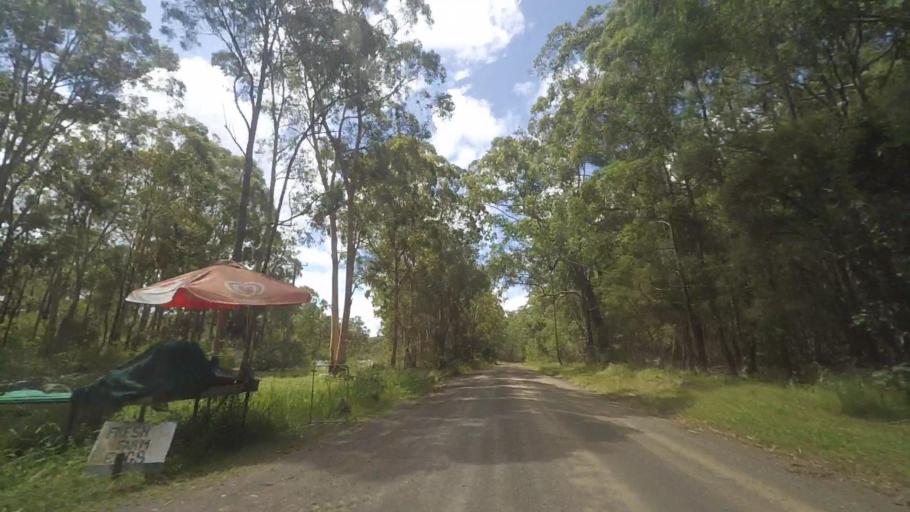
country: AU
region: New South Wales
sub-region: Great Lakes
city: Bulahdelah
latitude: -32.4938
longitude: 152.2764
